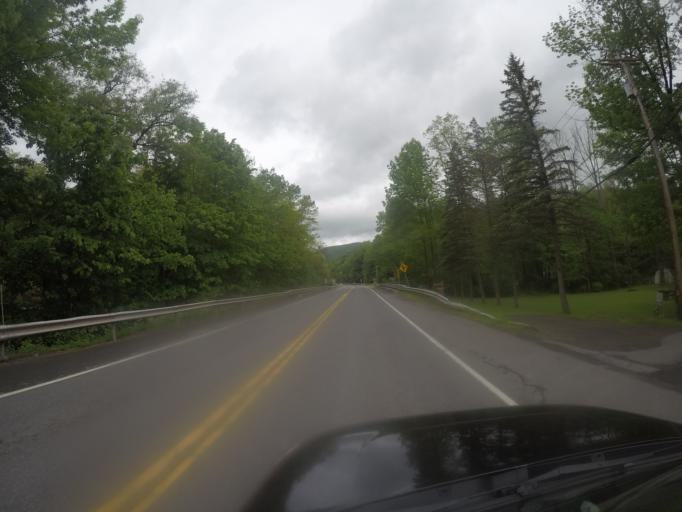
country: US
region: New York
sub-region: Ulster County
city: Shokan
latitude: 42.1124
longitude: -74.3582
